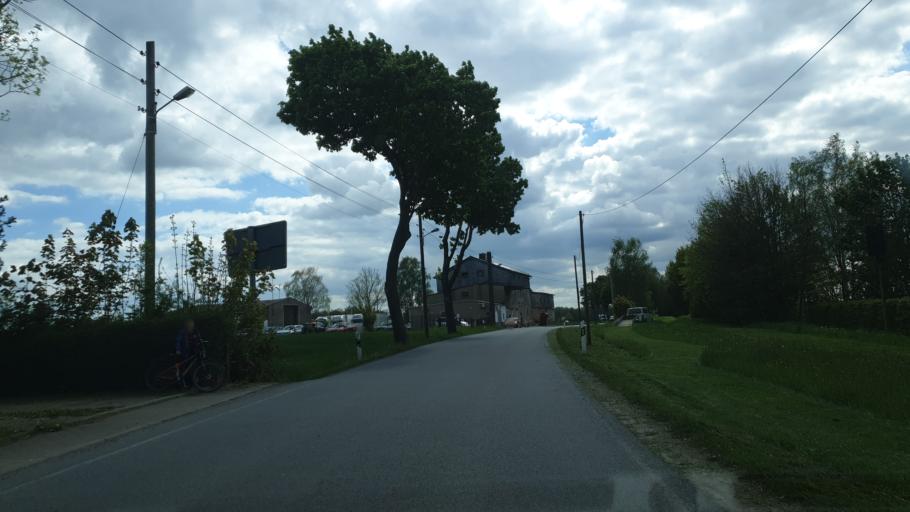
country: DE
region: Saxony
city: Niederdorf
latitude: 50.7732
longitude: 12.7872
